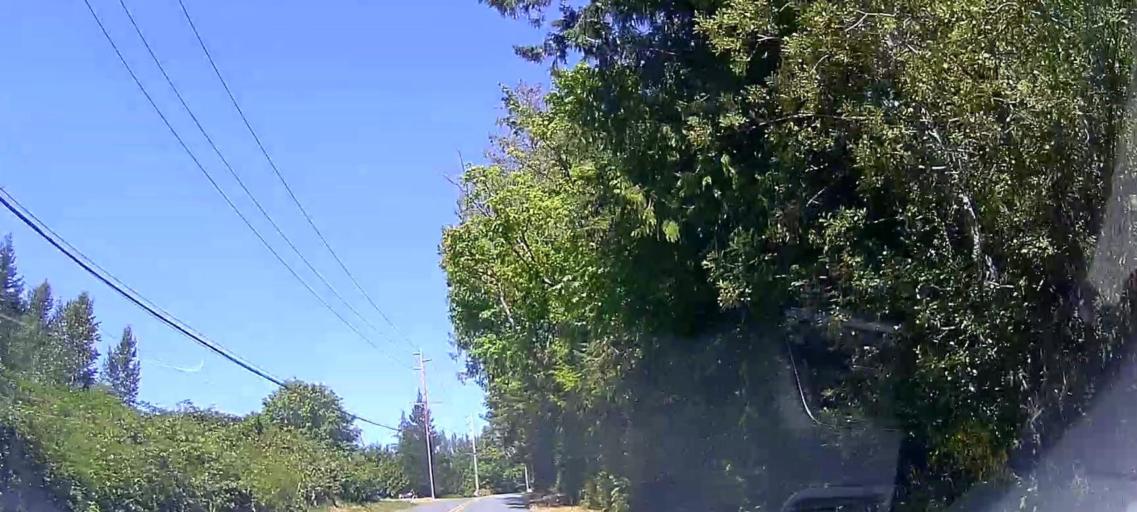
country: US
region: Washington
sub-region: Skagit County
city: Anacortes
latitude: 48.4500
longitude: -122.5664
